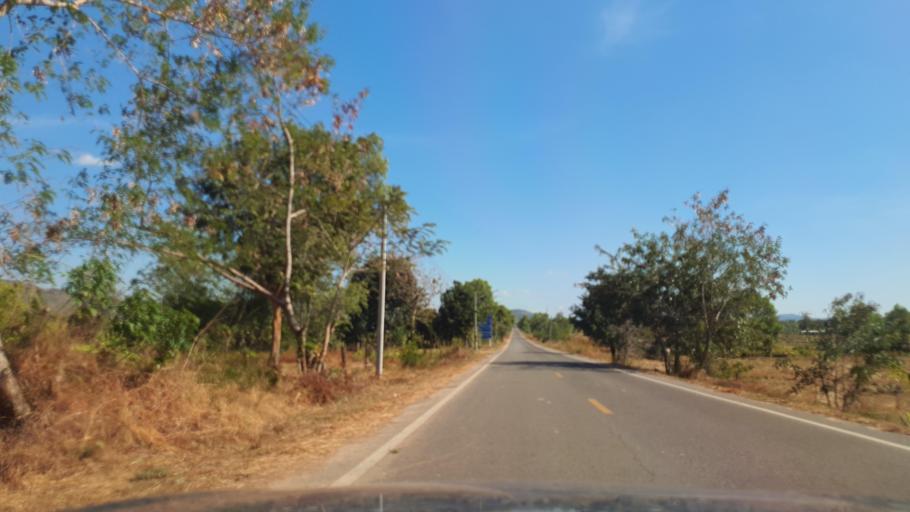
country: TH
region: Kalasin
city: Khao Wong
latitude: 16.7235
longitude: 104.1042
